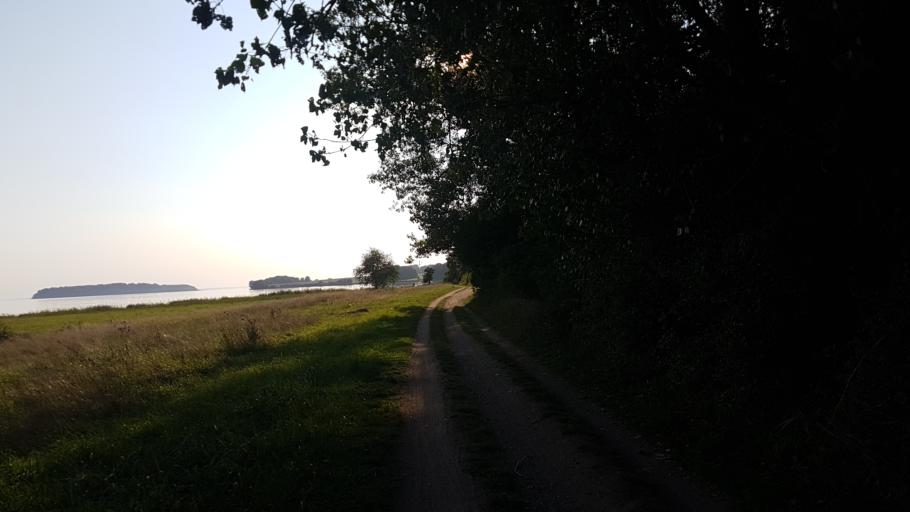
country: DE
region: Mecklenburg-Vorpommern
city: Ostseebad Binz
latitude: 54.3537
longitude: 13.5837
